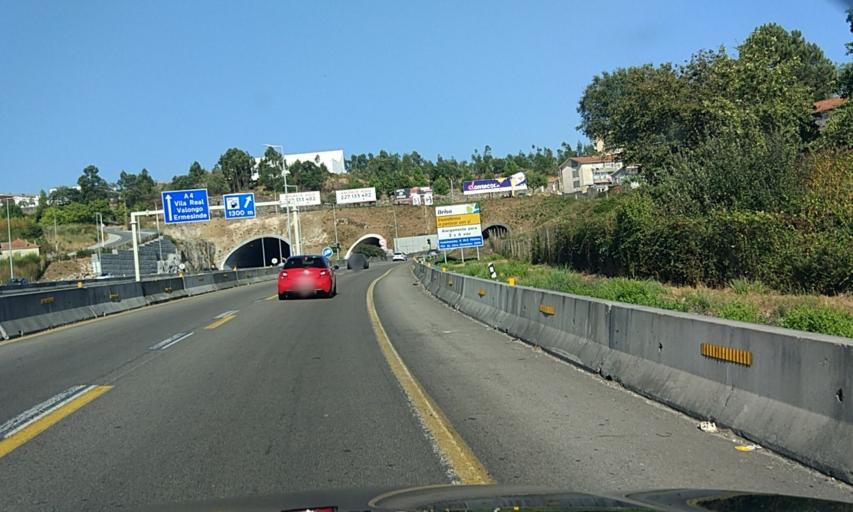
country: PT
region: Porto
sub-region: Maia
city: Pedroucos
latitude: 41.1982
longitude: -8.5808
